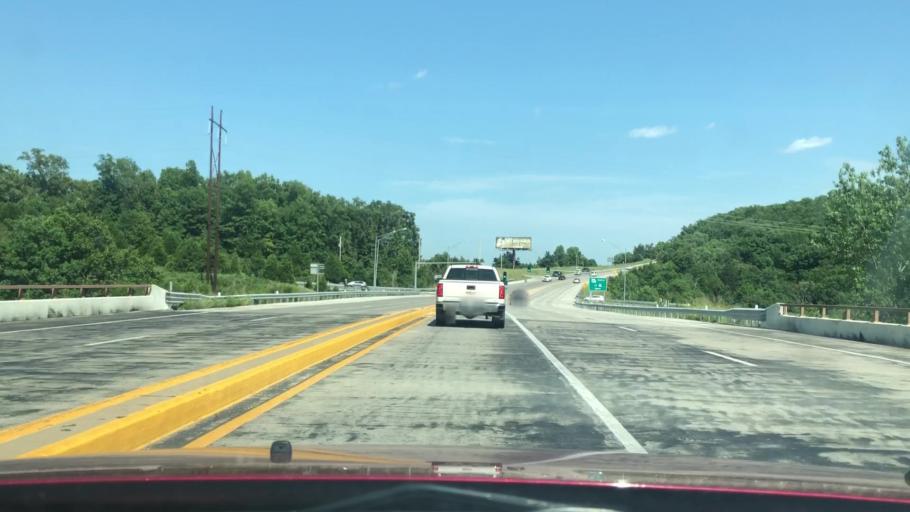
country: US
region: Missouri
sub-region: Taney County
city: Branson
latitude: 36.6755
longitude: -93.3173
